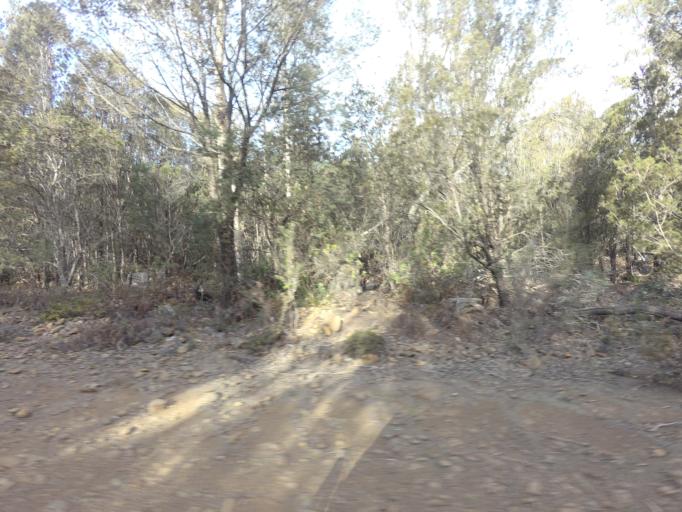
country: AU
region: Tasmania
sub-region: Break O'Day
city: St Helens
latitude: -41.8428
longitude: 148.0873
